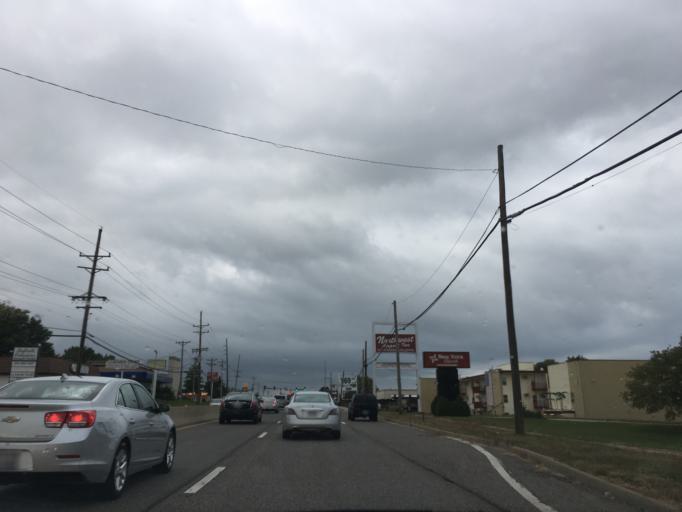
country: US
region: Missouri
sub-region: Saint Louis County
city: Saint Ann
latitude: 38.7291
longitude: -90.4052
